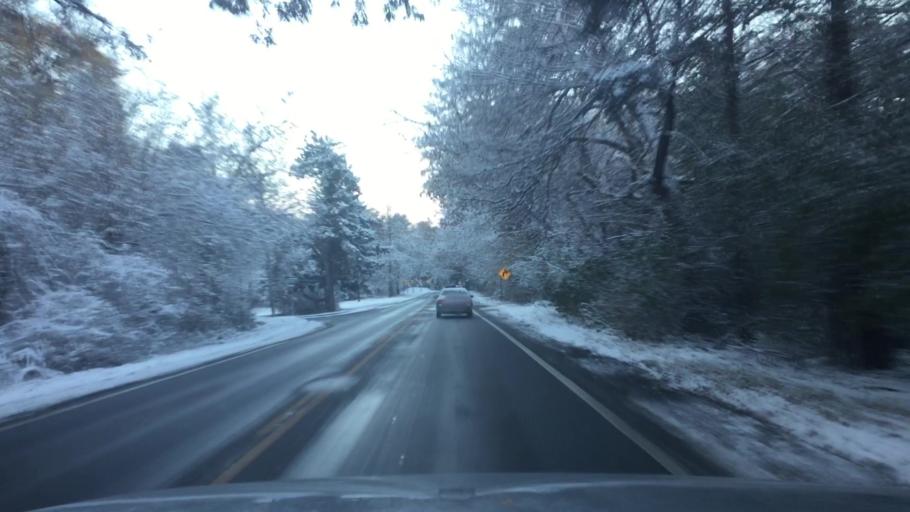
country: US
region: Michigan
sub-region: Oakland County
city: Wolverine Lake
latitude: 42.5917
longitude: -83.4357
